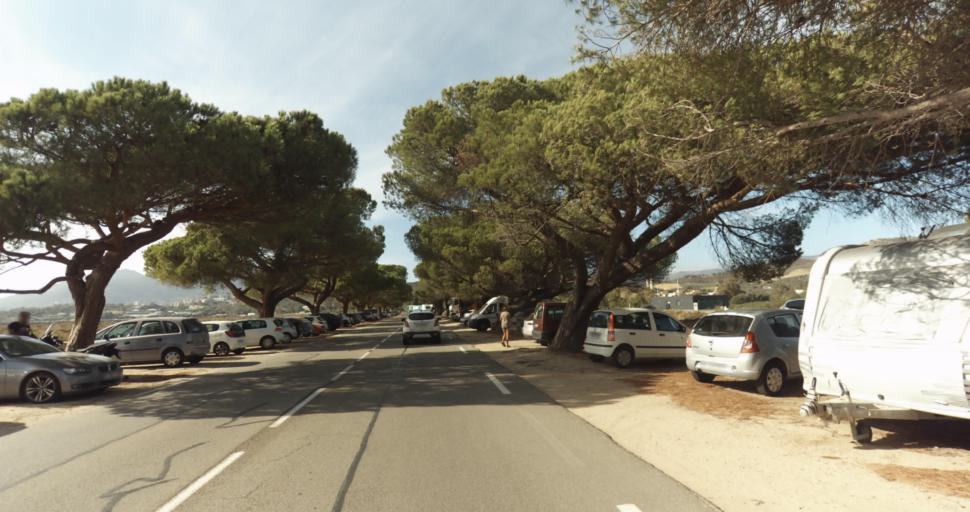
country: FR
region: Corsica
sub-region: Departement de la Corse-du-Sud
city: Ajaccio
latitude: 41.9227
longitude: 8.7853
